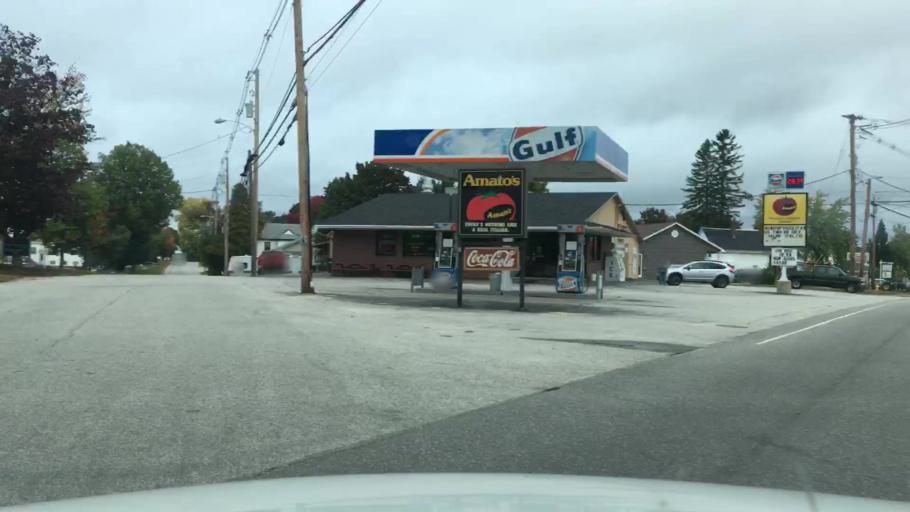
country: US
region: Maine
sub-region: Oxford County
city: Norway
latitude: 44.2090
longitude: -70.5307
